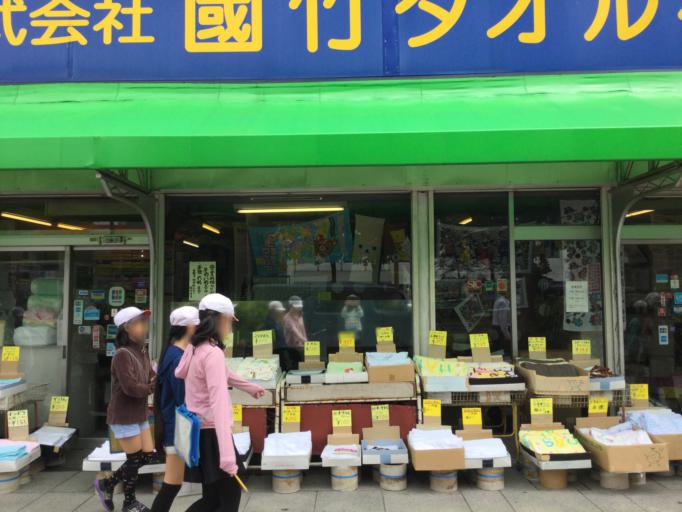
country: JP
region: Hokkaido
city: Sapporo
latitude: 43.0583
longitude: 141.3414
